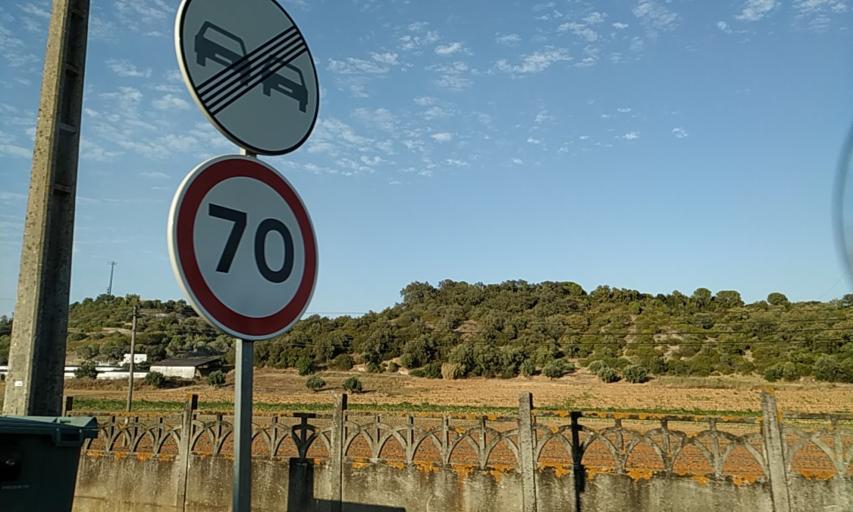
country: PT
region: Santarem
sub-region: Alcanena
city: Alcanena
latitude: 39.3736
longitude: -8.6596
